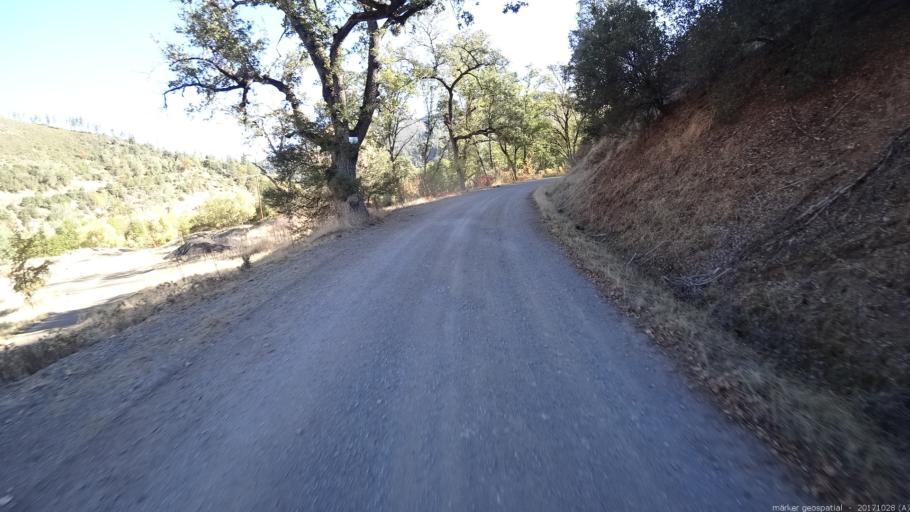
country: US
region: California
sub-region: Trinity County
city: Lewiston
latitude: 40.7153
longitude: -122.6341
